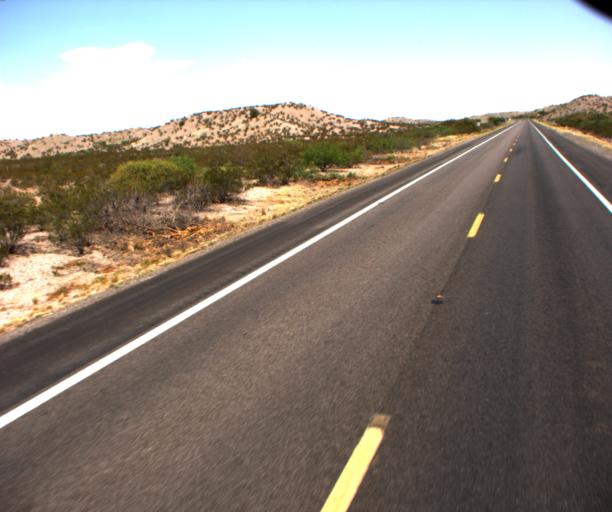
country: US
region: New Mexico
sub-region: Hidalgo County
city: Lordsburg
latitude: 32.6502
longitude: -109.0533
